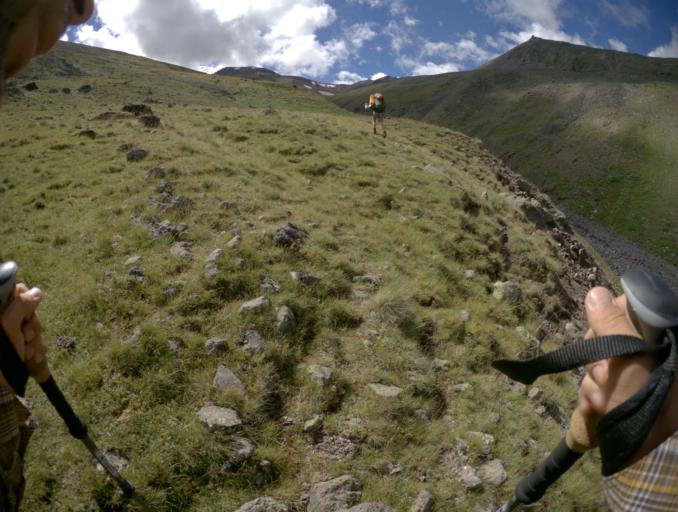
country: RU
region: Kabardino-Balkariya
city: Terskol
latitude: 43.3912
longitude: 42.3618
